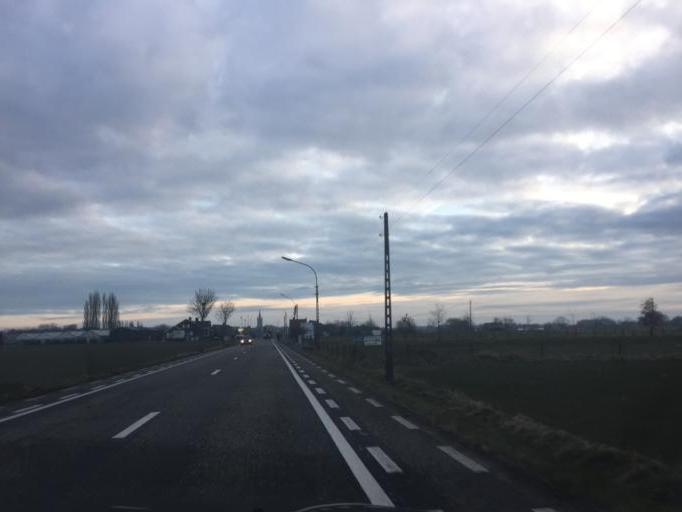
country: BE
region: Flanders
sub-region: Provincie West-Vlaanderen
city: Hooglede
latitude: 50.9697
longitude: 3.0693
